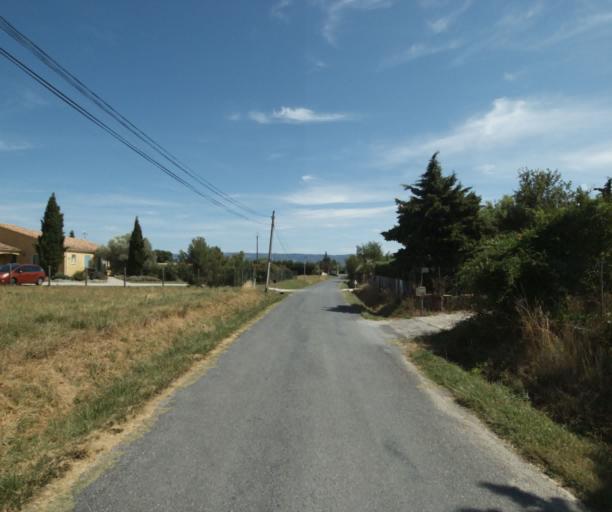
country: FR
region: Midi-Pyrenees
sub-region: Departement du Tarn
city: Puylaurens
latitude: 43.5366
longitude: 2.0132
